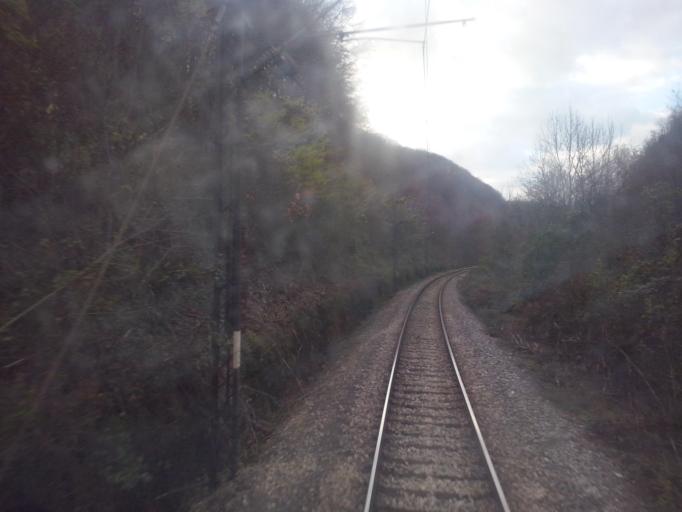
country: RS
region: Central Serbia
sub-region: Zlatiborski Okrug
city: Kosjeric
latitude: 43.9593
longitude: 19.9729
